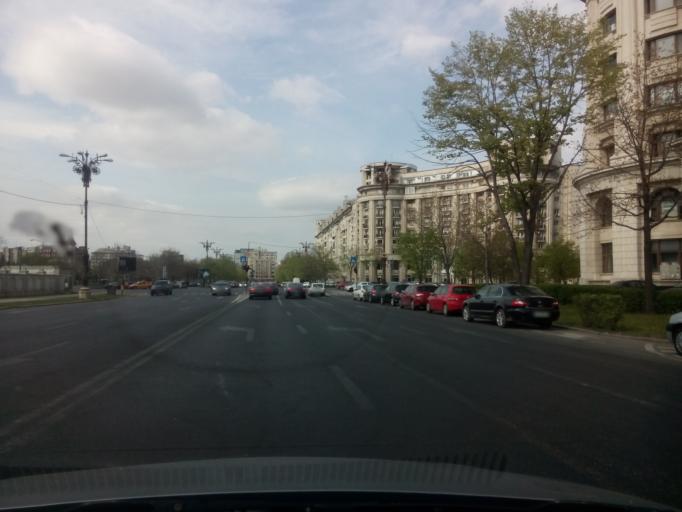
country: RO
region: Bucuresti
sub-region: Municipiul Bucuresti
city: Bucuresti
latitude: 44.4289
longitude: 26.0912
